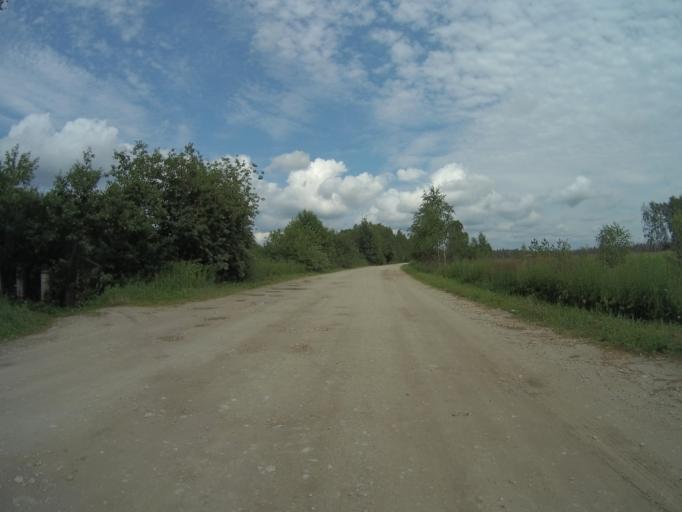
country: RU
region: Vladimir
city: Orgtrud
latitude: 56.2452
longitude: 40.6923
